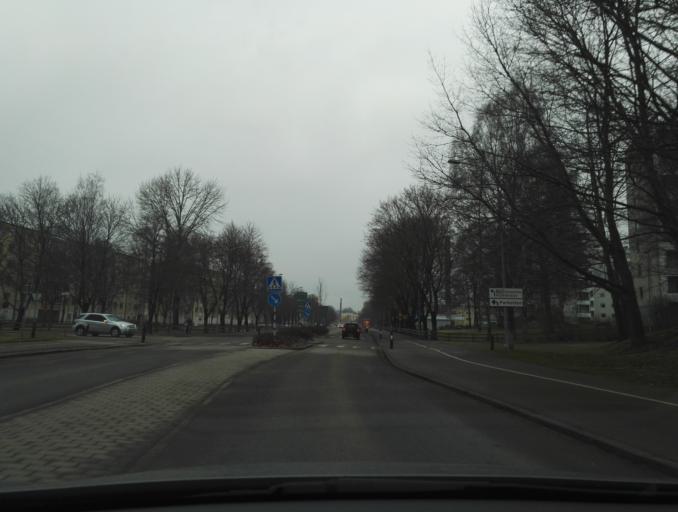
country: SE
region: Kronoberg
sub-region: Vaxjo Kommun
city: Vaexjoe
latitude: 56.8860
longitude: 14.8006
